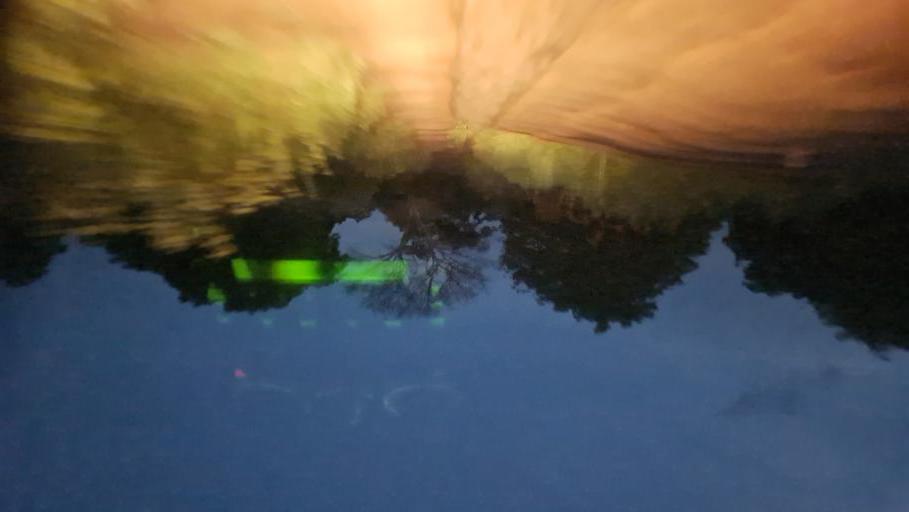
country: MZ
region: Nampula
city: Nampula
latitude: -14.6738
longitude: 39.8323
